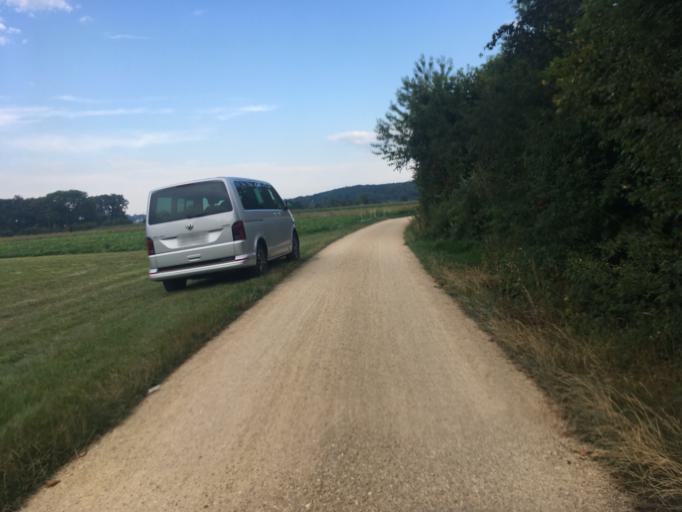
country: CH
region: Solothurn
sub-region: Bezirk Lebern
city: Langendorf
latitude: 47.2041
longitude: 7.4955
